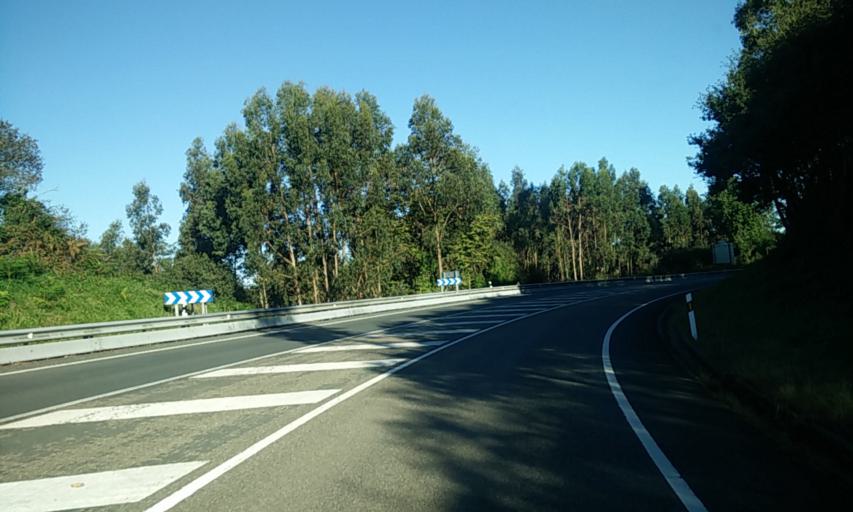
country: ES
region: Cantabria
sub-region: Provincia de Cantabria
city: San Vicente de la Barquera
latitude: 43.3744
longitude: -4.3729
